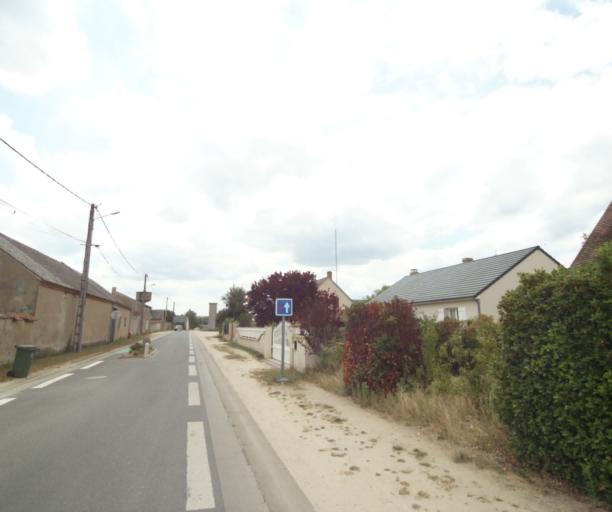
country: FR
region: Centre
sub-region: Departement du Loiret
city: Saint-Hilaire-Saint-Mesmin
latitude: 47.8586
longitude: 1.8479
